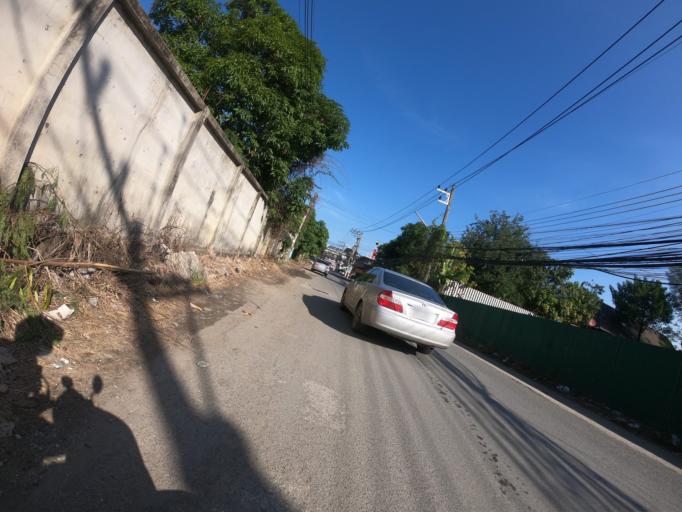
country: TH
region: Chiang Mai
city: Chiang Mai
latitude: 18.8102
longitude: 98.9902
